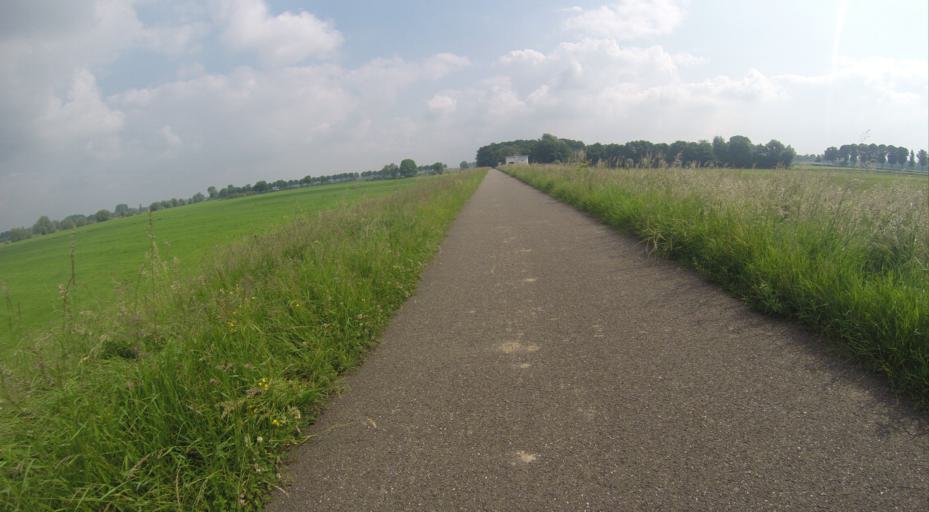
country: NL
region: Gelderland
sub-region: Gemeente Brummen
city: Brummen
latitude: 52.0725
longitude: 6.1713
